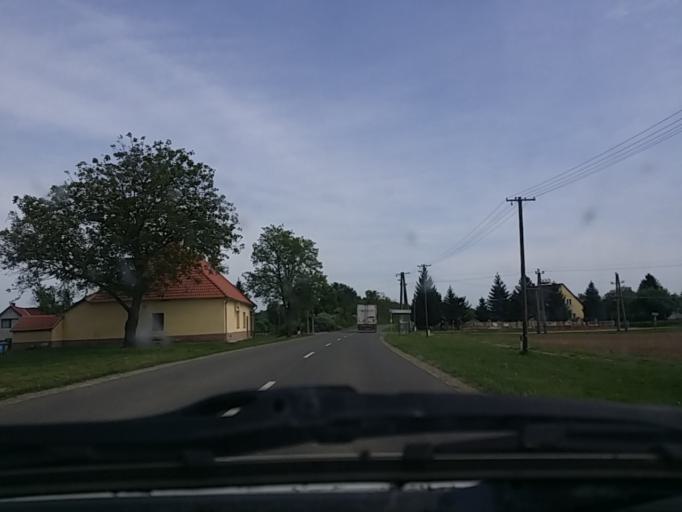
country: HU
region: Baranya
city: Vajszlo
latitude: 45.8766
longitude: 17.9449
